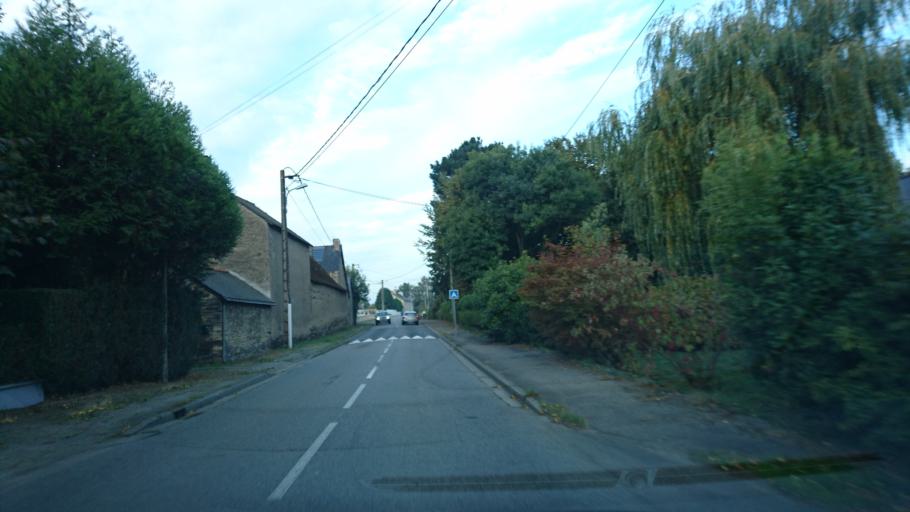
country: FR
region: Brittany
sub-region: Departement d'Ille-et-Vilaine
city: Redon
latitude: 47.6730
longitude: -2.0749
